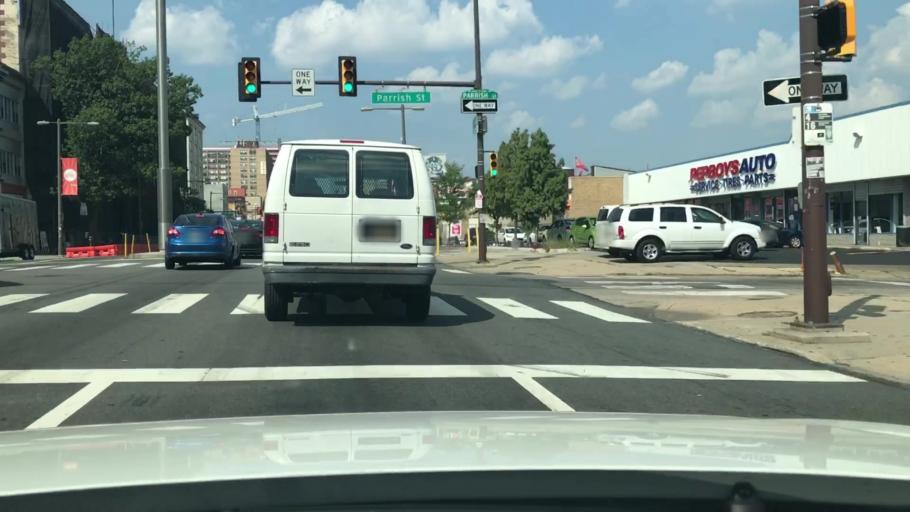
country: US
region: Pennsylvania
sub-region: Philadelphia County
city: Philadelphia
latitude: 39.9687
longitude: -75.1600
